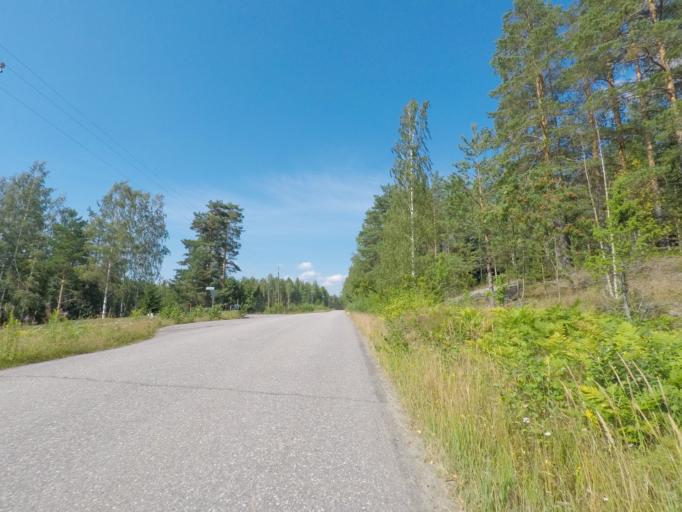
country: FI
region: Southern Savonia
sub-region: Mikkeli
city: Puumala
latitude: 61.4462
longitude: 28.1606
